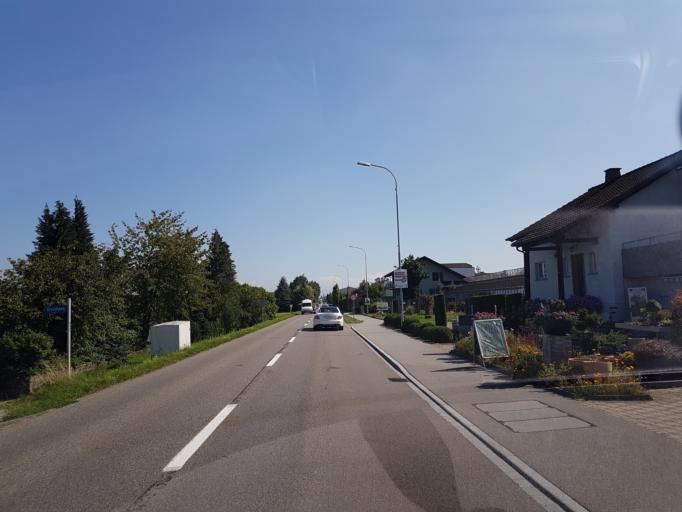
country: CH
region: Aargau
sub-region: Bezirk Muri
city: Buttwil
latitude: 47.2980
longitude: 8.3171
